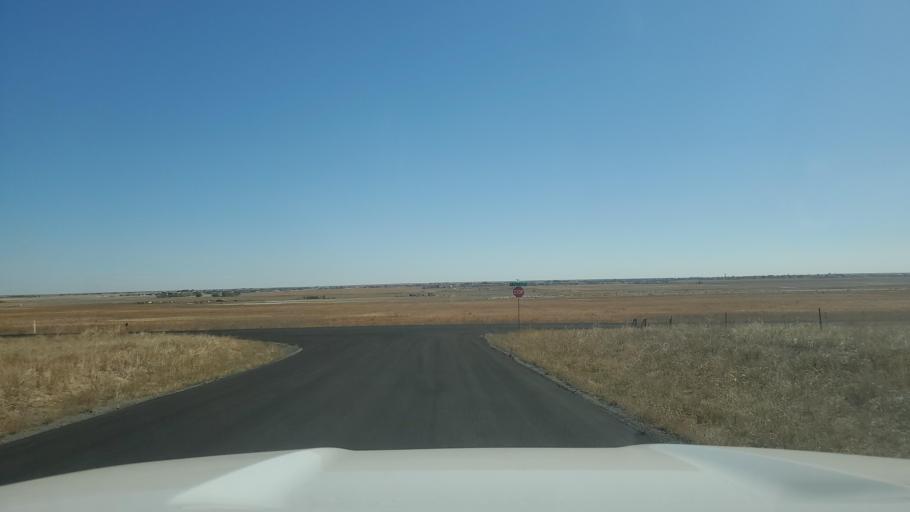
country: US
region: Colorado
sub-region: Adams County
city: Bennett
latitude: 39.7599
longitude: -104.3778
